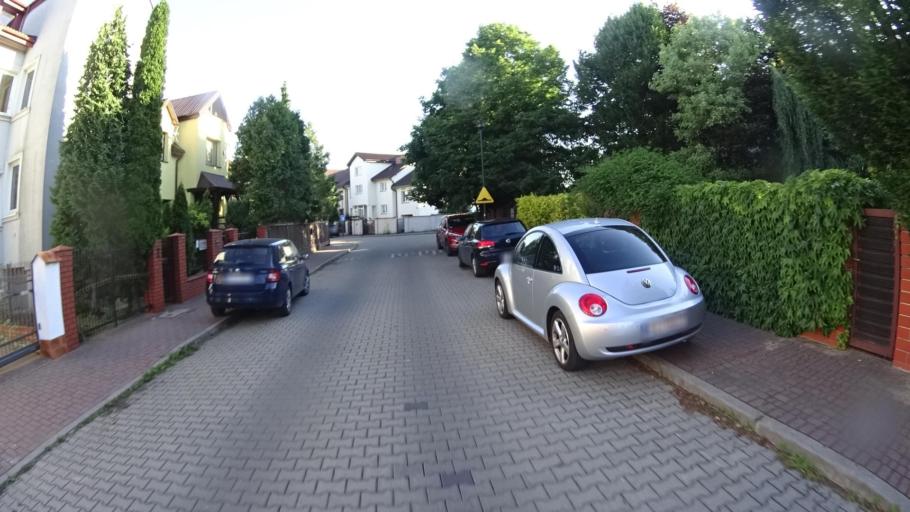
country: PL
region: Masovian Voivodeship
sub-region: Warszawa
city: Bemowo
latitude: 52.2640
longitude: 20.9135
